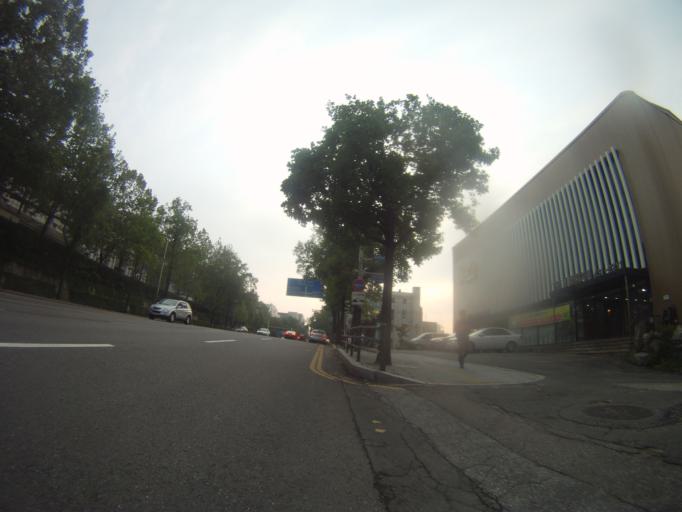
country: KR
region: Incheon
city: Incheon
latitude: 37.4572
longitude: 126.6958
